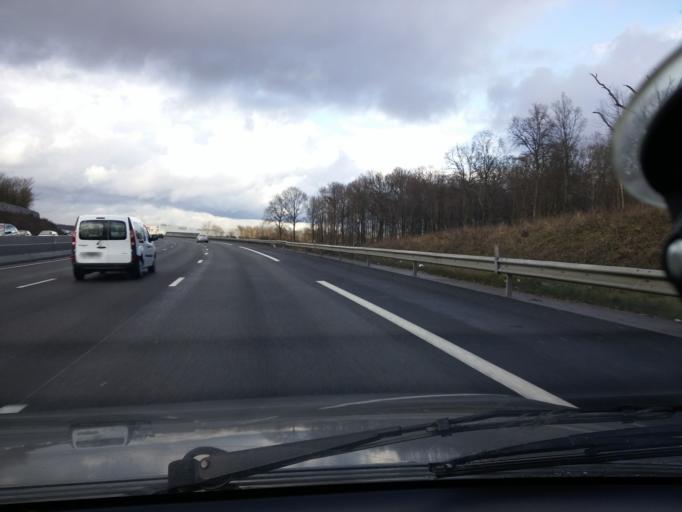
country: FR
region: Ile-de-France
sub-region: Departement de Seine-et-Marne
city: Emerainville
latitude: 48.8113
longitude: 2.6299
